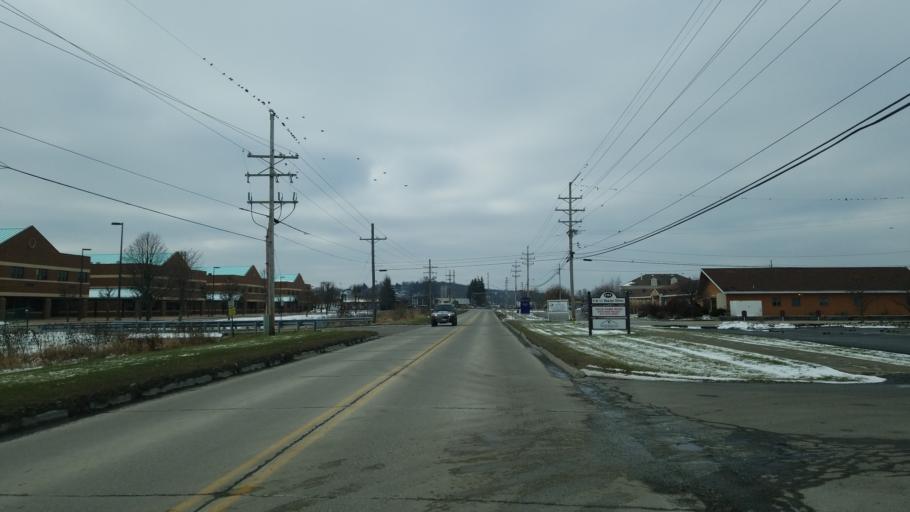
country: US
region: Pennsylvania
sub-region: Clearfield County
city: DuBois
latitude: 41.1236
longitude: -78.7531
